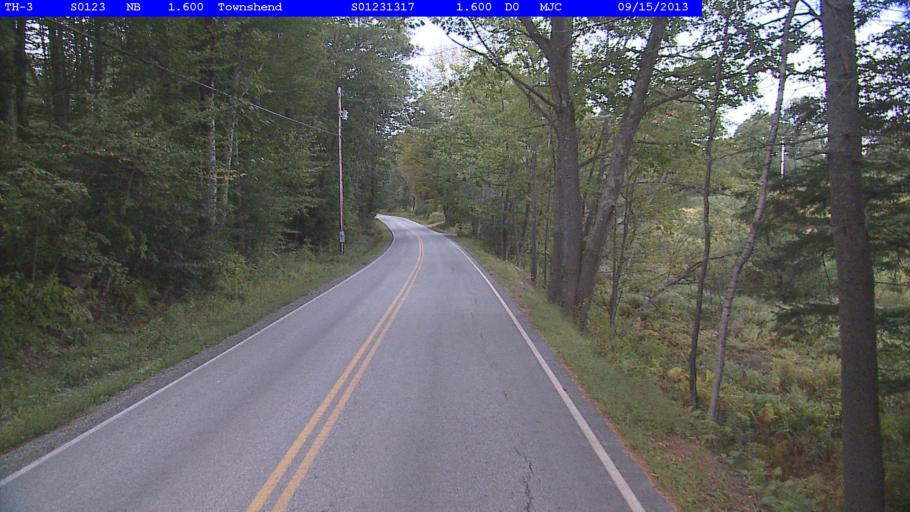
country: US
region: Vermont
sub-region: Windham County
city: Newfane
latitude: 43.1058
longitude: -72.7087
